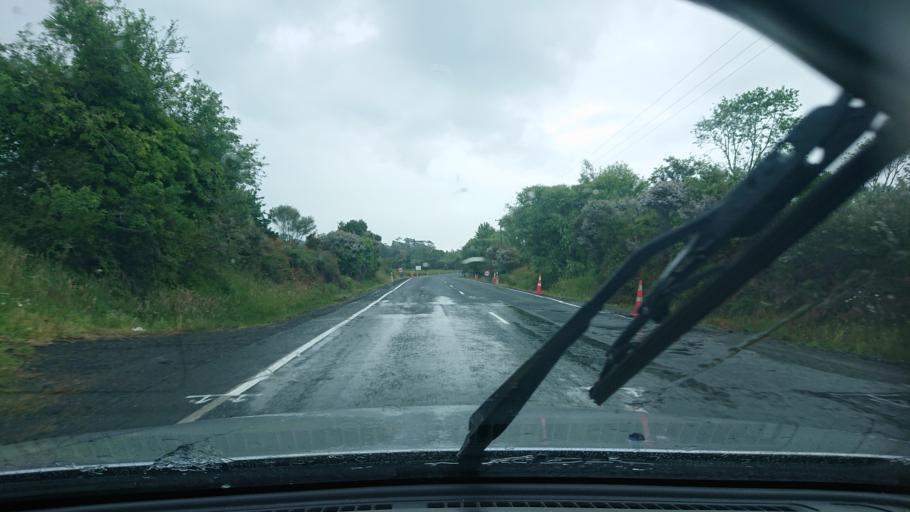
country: NZ
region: Auckland
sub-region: Auckland
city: Wellsford
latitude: -36.3208
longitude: 174.4866
